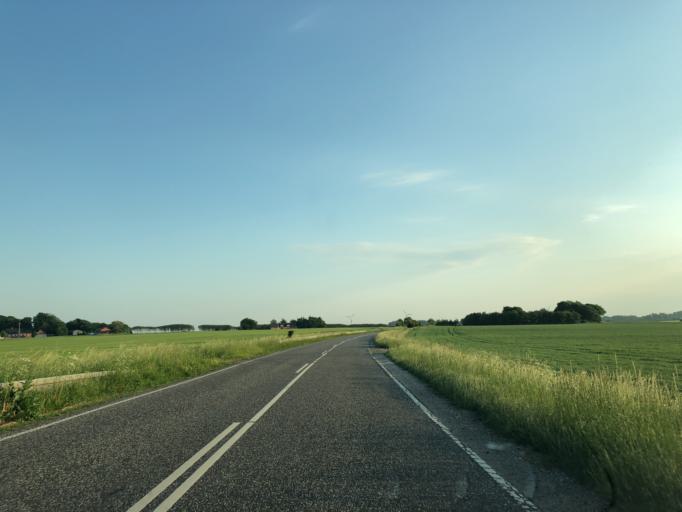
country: DK
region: Central Jutland
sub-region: Struer Kommune
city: Struer
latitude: 56.4427
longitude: 8.5320
